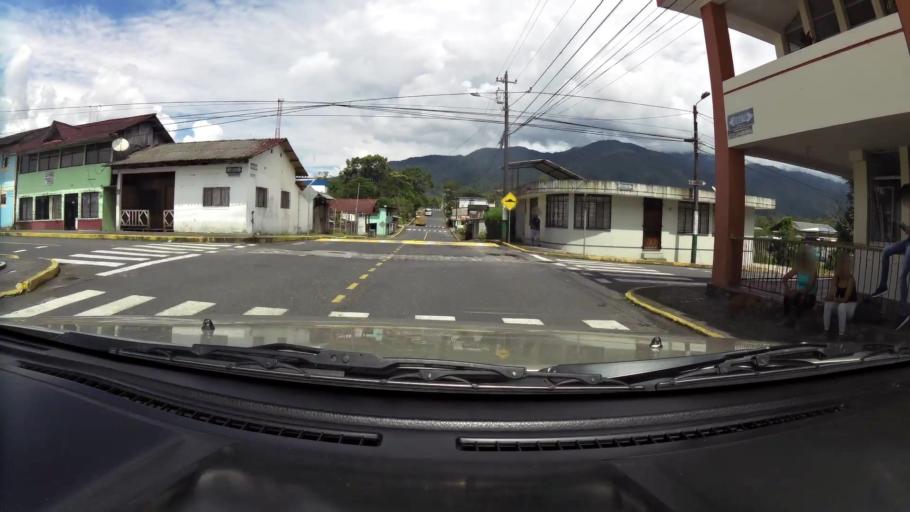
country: EC
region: Pastaza
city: Puyo
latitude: -1.4601
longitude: -78.1140
